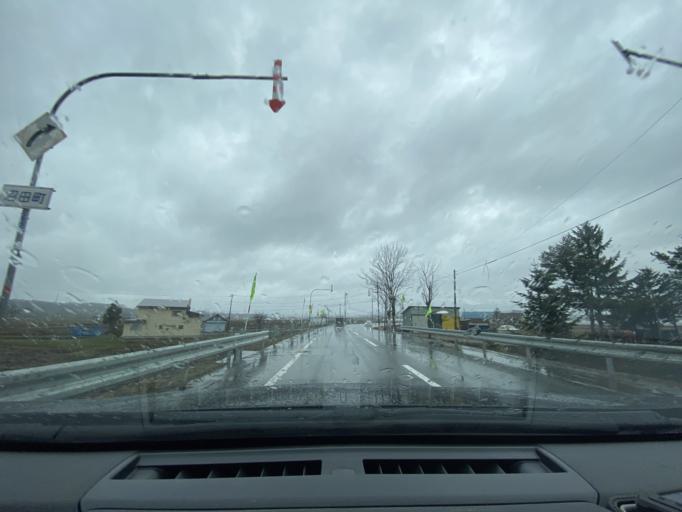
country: JP
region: Hokkaido
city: Fukagawa
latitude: 43.8094
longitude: 142.0134
